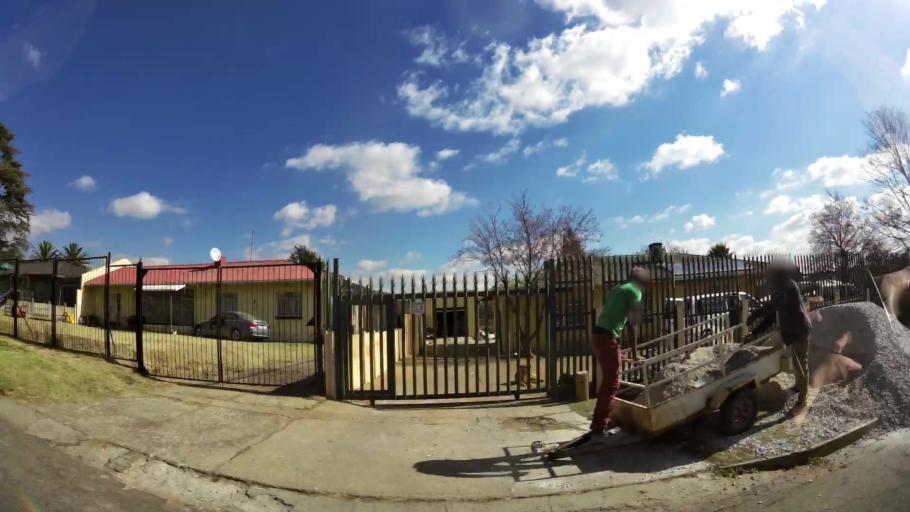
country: ZA
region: Gauteng
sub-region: West Rand District Municipality
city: Krugersdorp
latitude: -26.1208
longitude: 27.8054
